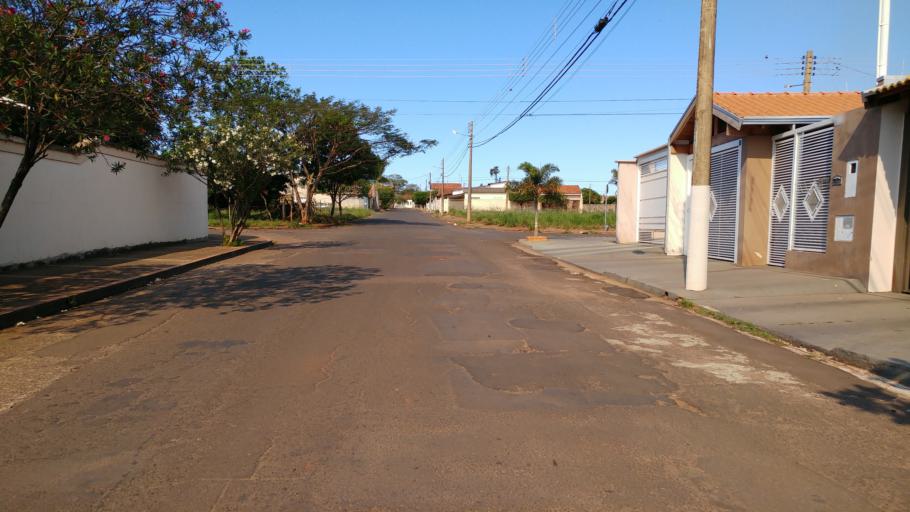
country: BR
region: Sao Paulo
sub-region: Paraguacu Paulista
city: Paraguacu Paulista
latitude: -22.4148
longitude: -50.5895
